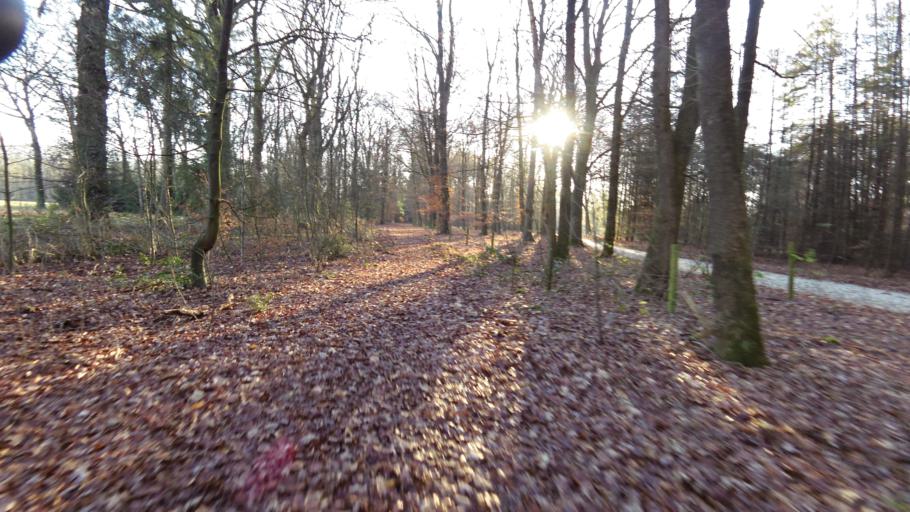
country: NL
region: Gelderland
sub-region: Gemeente Barneveld
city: Garderen
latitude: 52.2173
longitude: 5.7228
